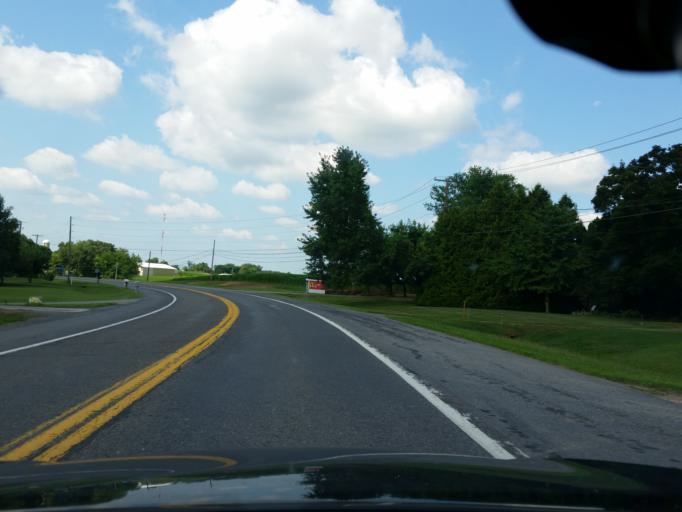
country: US
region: Pennsylvania
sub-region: Dauphin County
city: Matamoras
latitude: 40.4861
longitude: -76.8995
